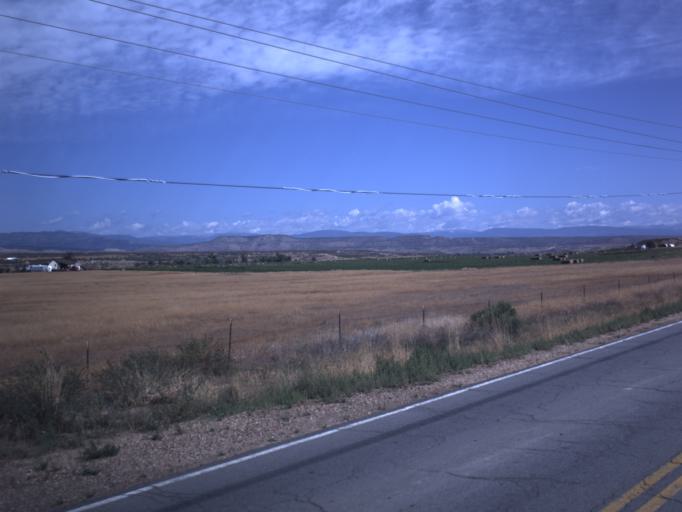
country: US
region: Utah
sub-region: Duchesne County
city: Duchesne
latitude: 40.1810
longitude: -110.3987
